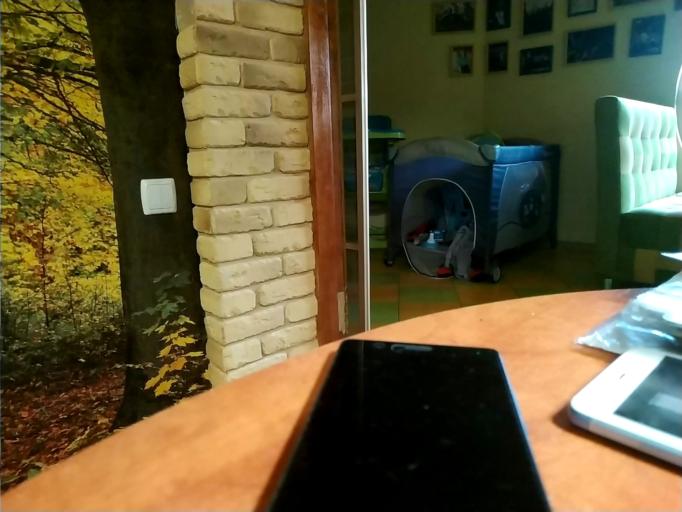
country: RU
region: Kaluga
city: Khvastovichi
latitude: 53.6356
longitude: 35.4559
